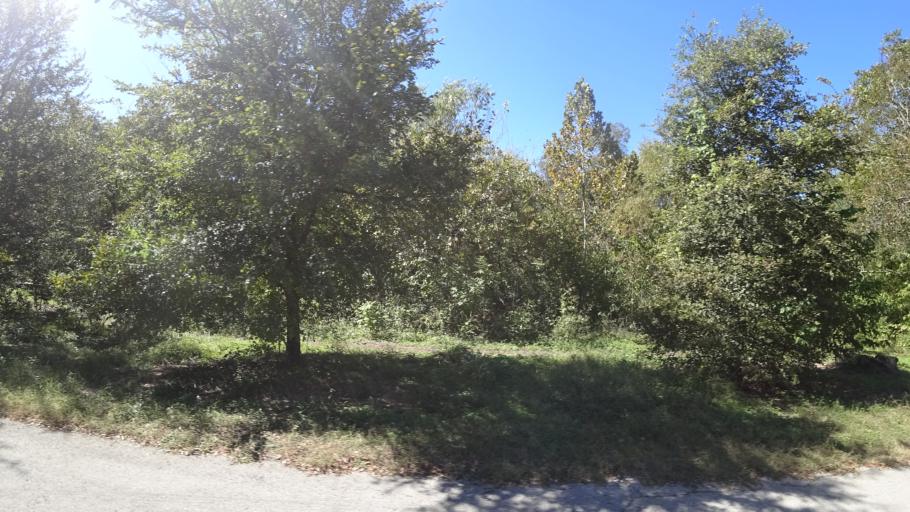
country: US
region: Texas
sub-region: Travis County
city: Austin
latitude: 30.2929
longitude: -97.7115
